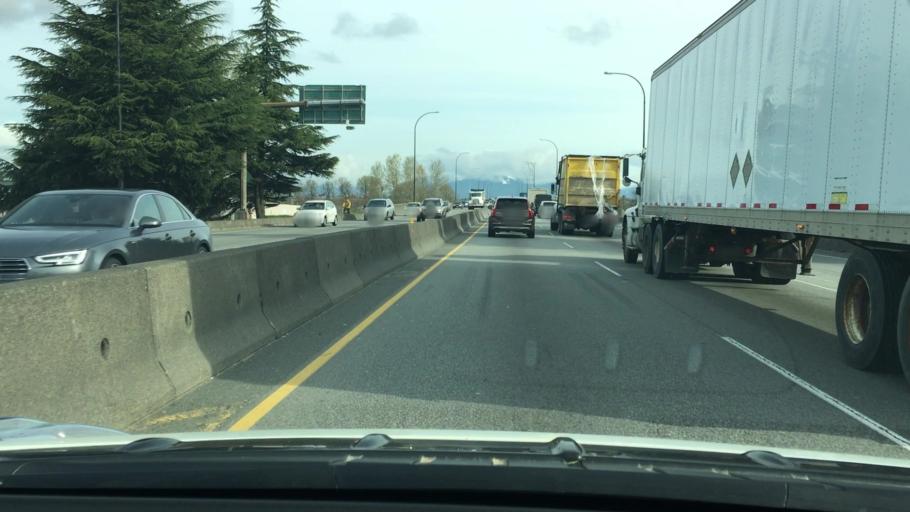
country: CA
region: British Columbia
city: Richmond
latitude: 49.1941
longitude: -123.0774
